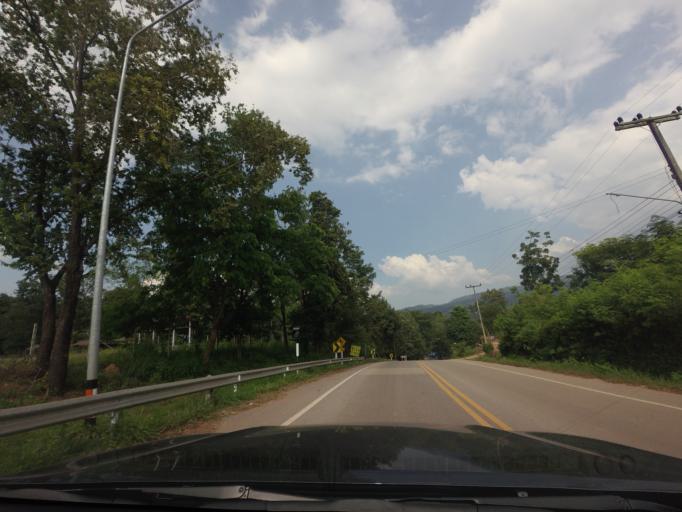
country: TH
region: Phitsanulok
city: Nakhon Thai
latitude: 17.0191
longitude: 100.9202
